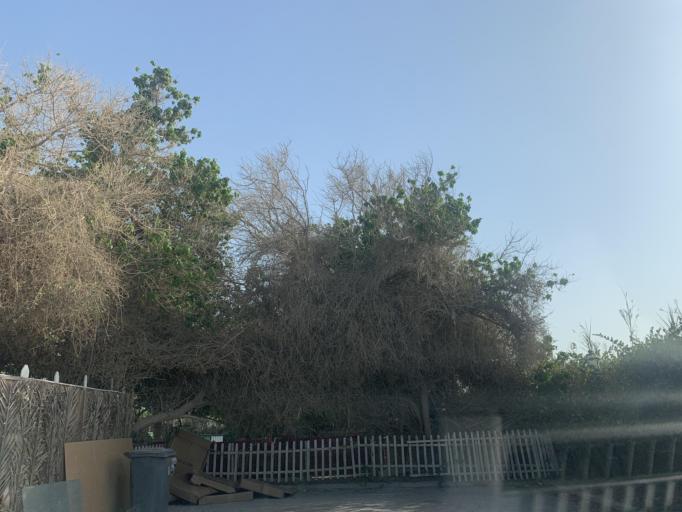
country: BH
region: Northern
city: Madinat `Isa
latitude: 26.1941
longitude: 50.4597
